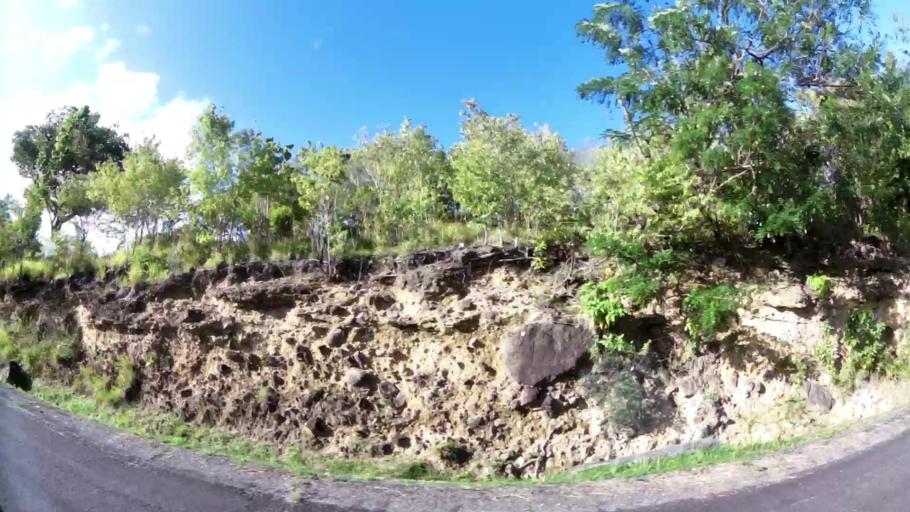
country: LC
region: Anse-la-Raye
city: Anse La Raye
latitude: 13.9232
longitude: -61.0429
